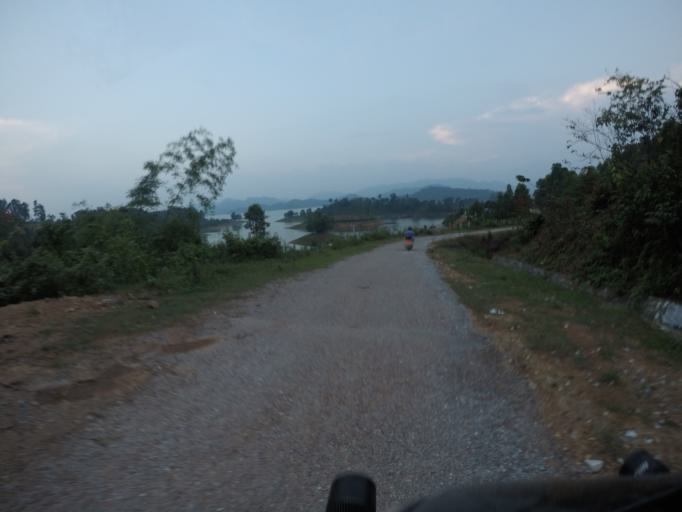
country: VN
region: Thai Nguyen
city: Chua Hang
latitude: 21.5842
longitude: 105.7100
